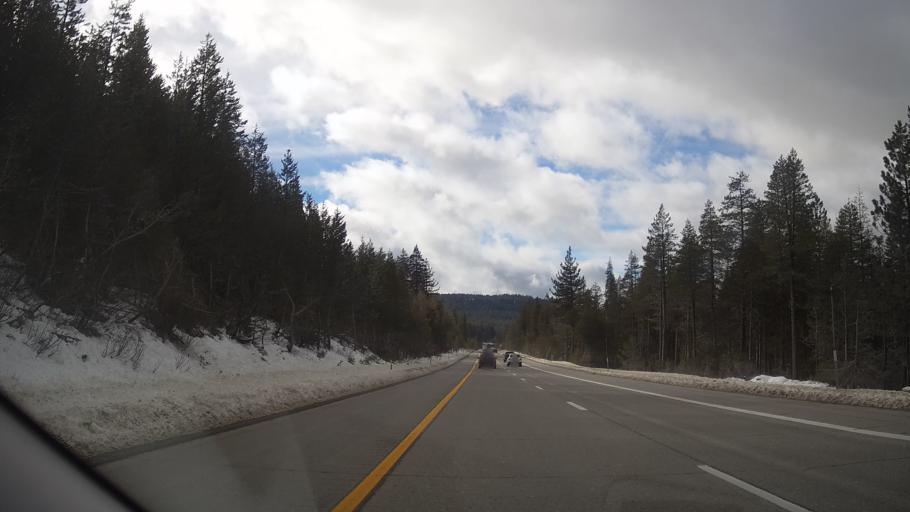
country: US
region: California
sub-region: Nevada County
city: Truckee
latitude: 39.3217
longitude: -120.4224
